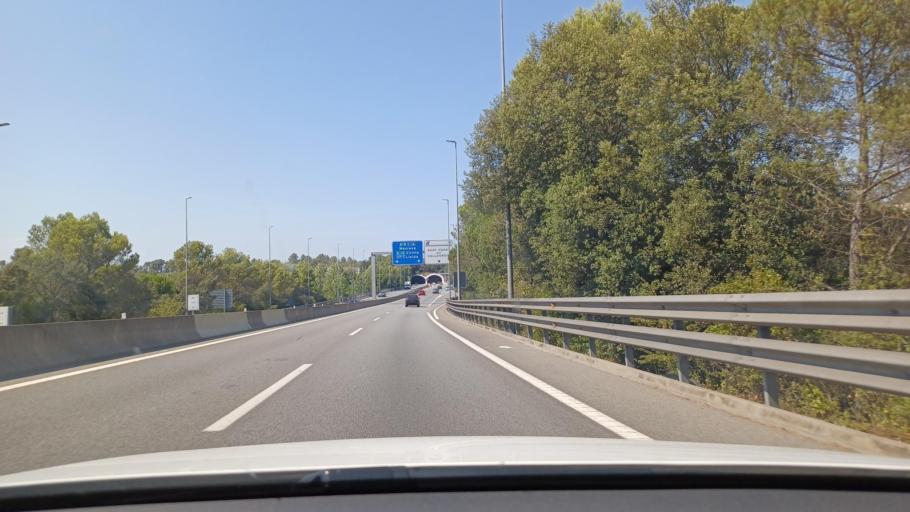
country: ES
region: Catalonia
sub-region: Provincia de Barcelona
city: Sant Cugat del Valles
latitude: 41.4462
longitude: 2.0695
